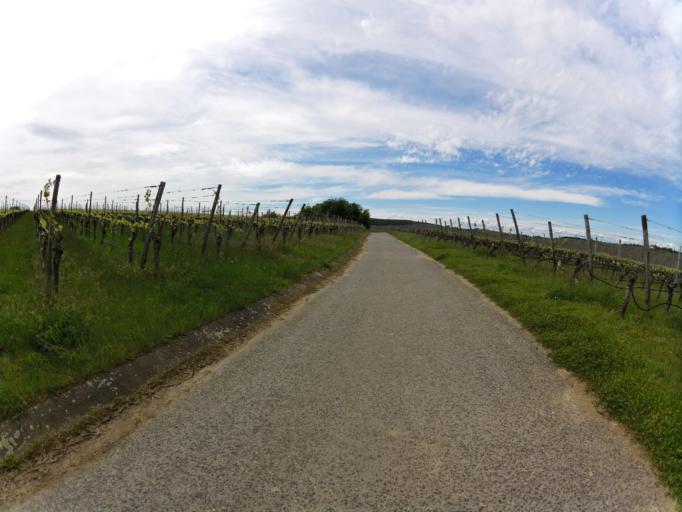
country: DE
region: Bavaria
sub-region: Regierungsbezirk Unterfranken
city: Nordheim
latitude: 49.8553
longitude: 10.1988
